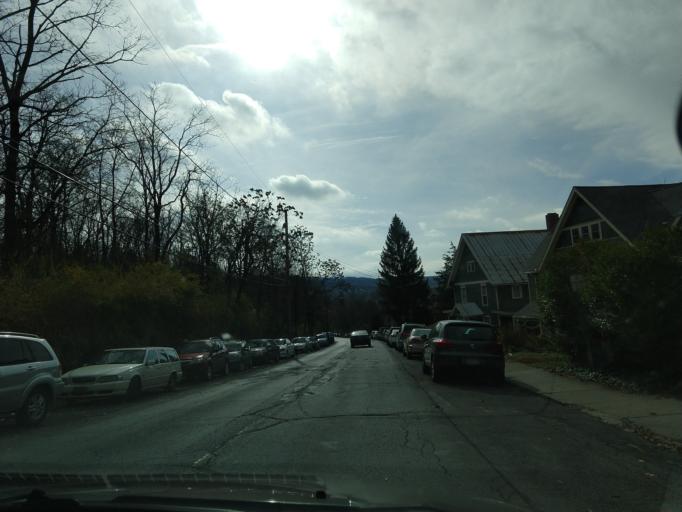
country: US
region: New York
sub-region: Tompkins County
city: Ithaca
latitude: 42.4481
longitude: -76.4929
